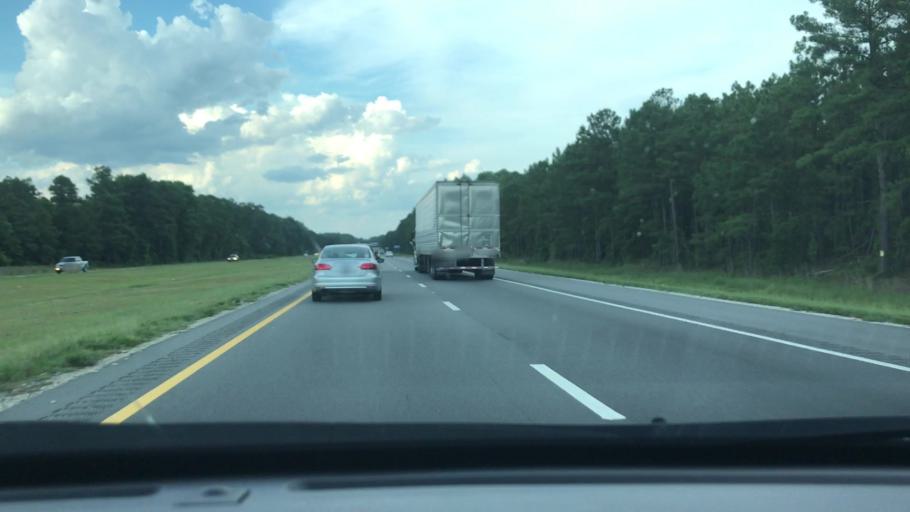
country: US
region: North Carolina
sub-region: Cumberland County
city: Hope Mills
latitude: 34.9490
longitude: -78.9042
